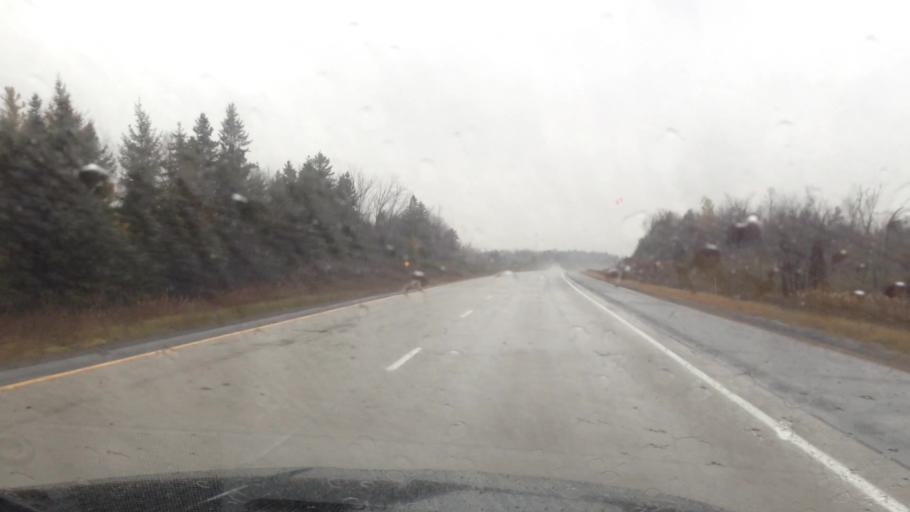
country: CA
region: Ontario
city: Hawkesbury
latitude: 45.4897
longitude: -74.6251
